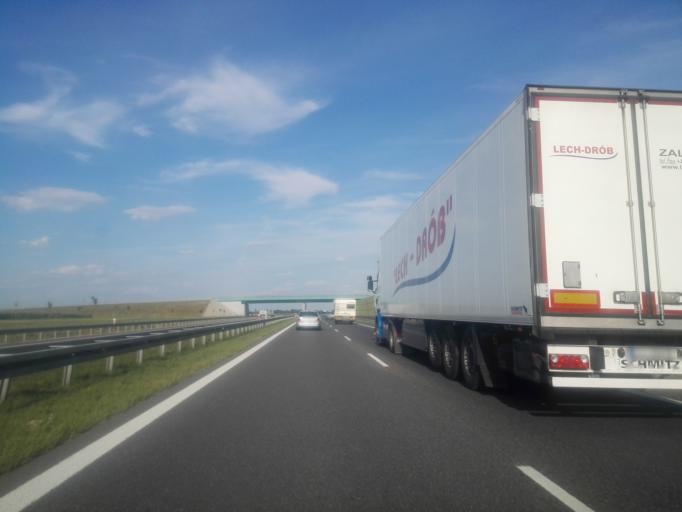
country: PL
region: Lower Silesian Voivodeship
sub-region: Powiat wroclawski
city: Dlugoleka
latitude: 51.2289
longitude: 17.2331
